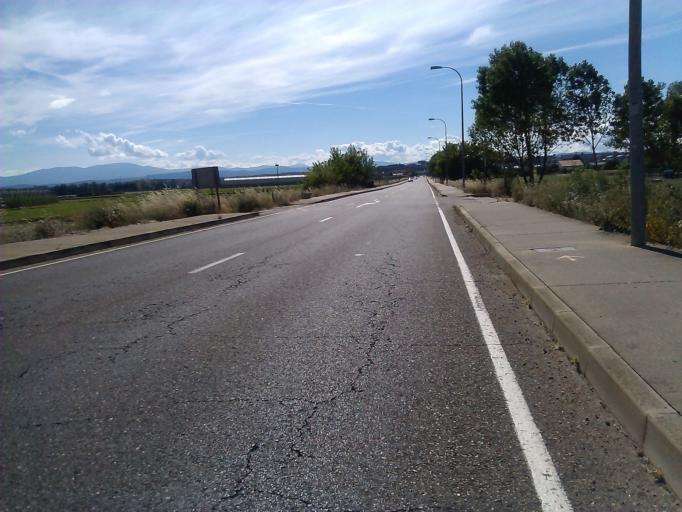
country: ES
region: Castille and Leon
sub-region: Provincia de Leon
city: San Justo de la Vega
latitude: 42.4539
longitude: -6.0252
